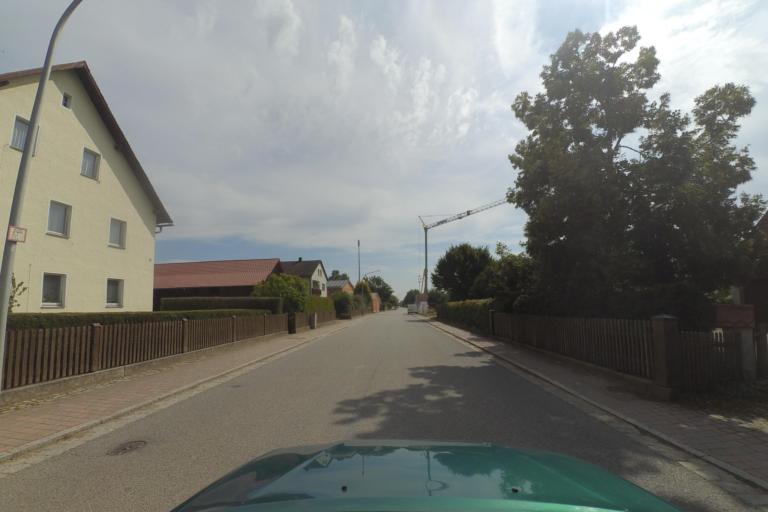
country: DE
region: Bavaria
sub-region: Upper Palatinate
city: Thalmassing
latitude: 48.9319
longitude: 12.1305
